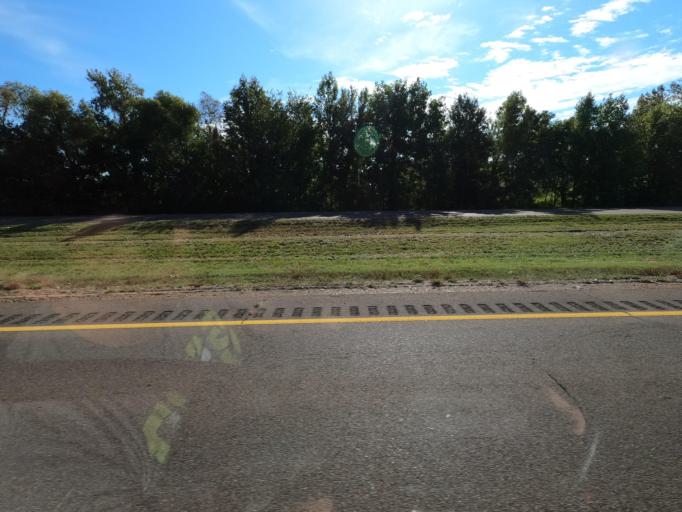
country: US
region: Tennessee
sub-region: Tipton County
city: Brighton
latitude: 35.4787
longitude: -89.7435
